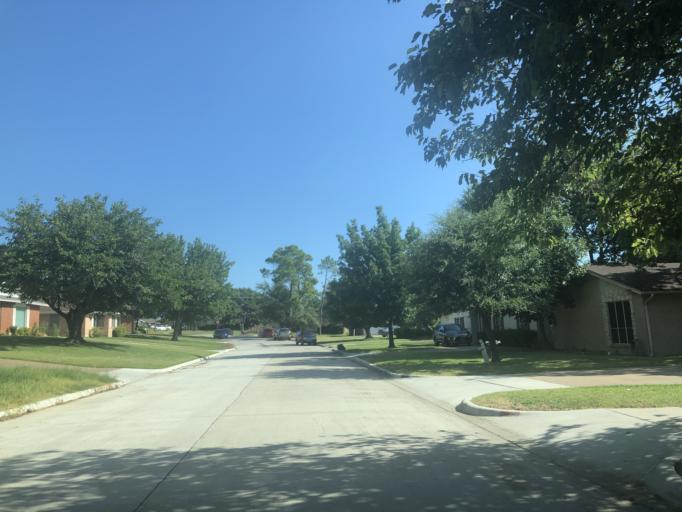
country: US
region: Texas
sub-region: Dallas County
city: Grand Prairie
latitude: 32.7568
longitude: -97.0229
